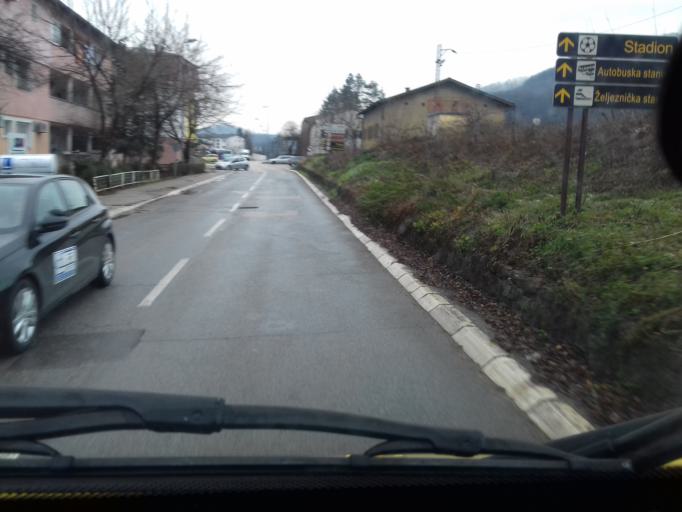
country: BA
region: Federation of Bosnia and Herzegovina
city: Maglaj
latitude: 44.5474
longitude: 18.0943
